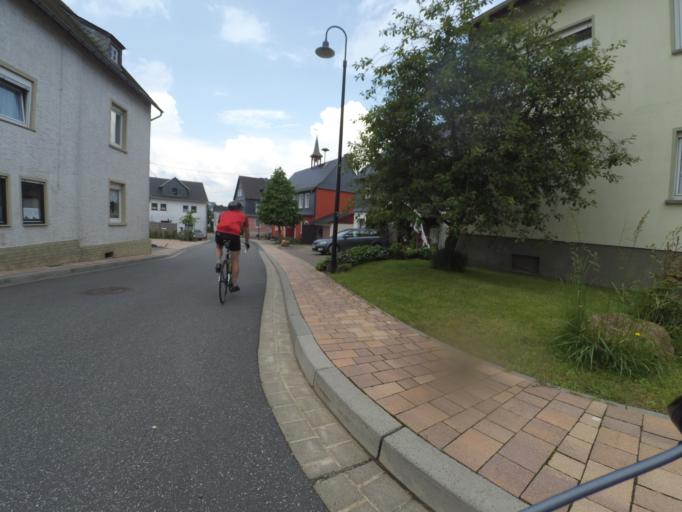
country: DE
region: Rheinland-Pfalz
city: Hollnich
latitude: 50.0728
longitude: 7.4880
